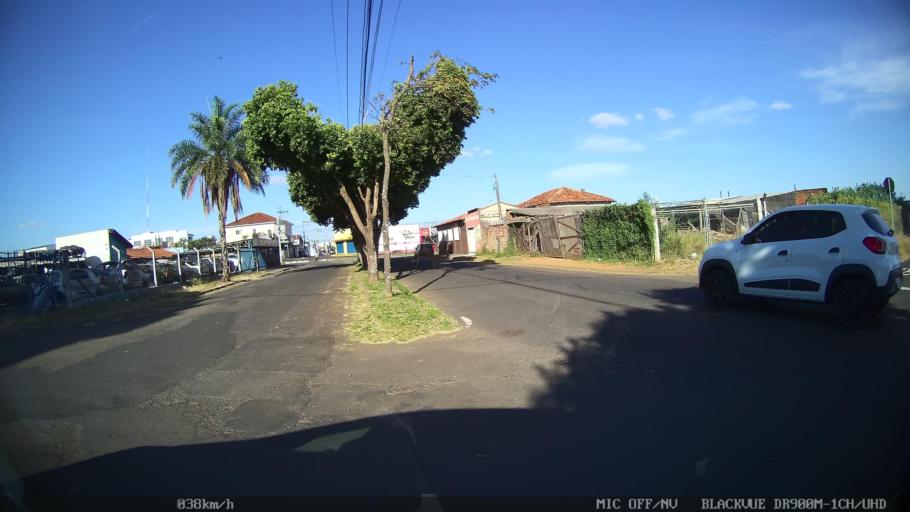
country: BR
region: Sao Paulo
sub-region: Franca
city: Franca
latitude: -20.5264
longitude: -47.4124
